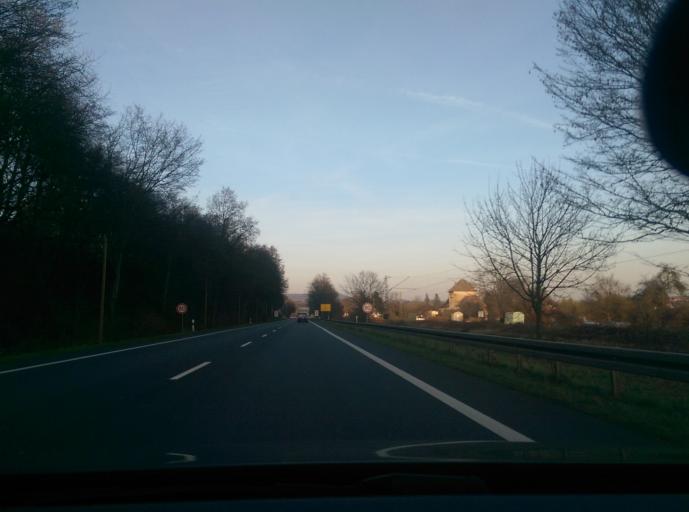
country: DE
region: Hesse
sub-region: Regierungsbezirk Kassel
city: Eschwege
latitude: 51.1515
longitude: 9.9828
